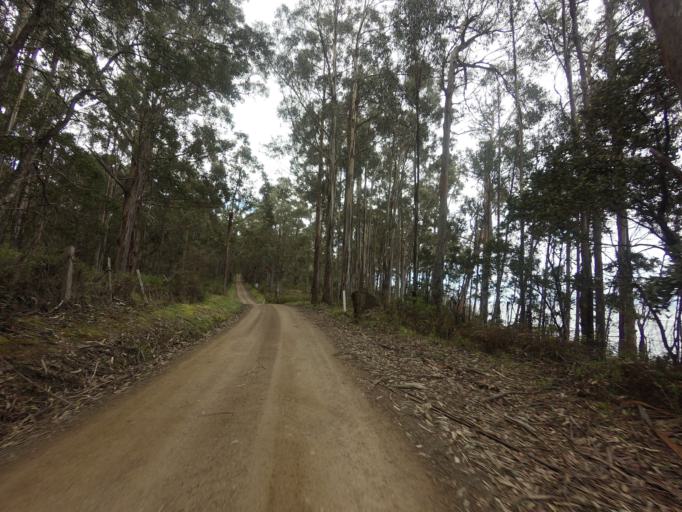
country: AU
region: Tasmania
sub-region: Huon Valley
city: Geeveston
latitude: -43.4196
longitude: 147.0140
